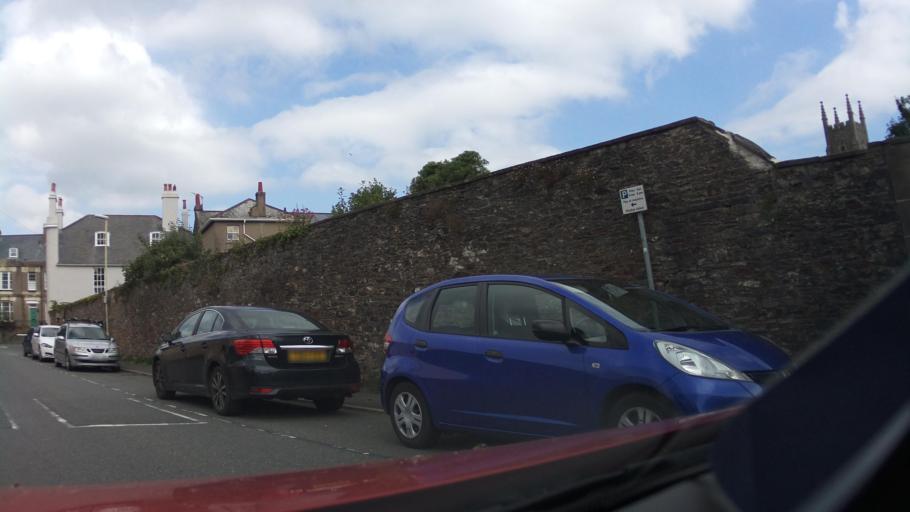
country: GB
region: England
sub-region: Devon
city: Totnes
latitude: 50.4297
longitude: -3.6801
